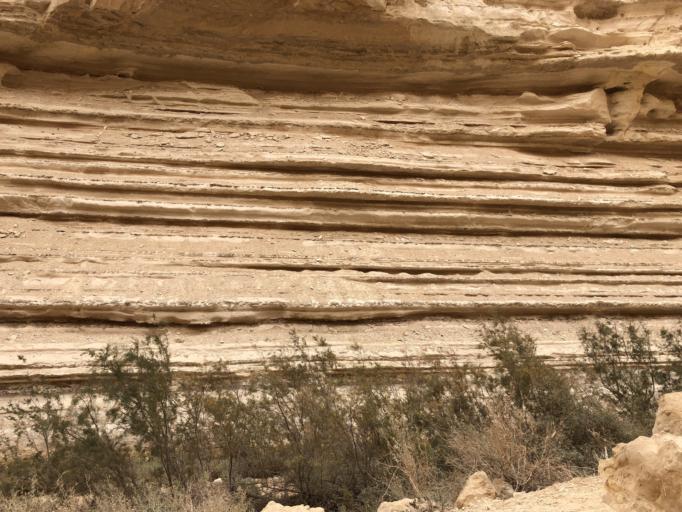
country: IL
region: Southern District
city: Midreshet Ben-Gurion
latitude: 30.8279
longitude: 34.7658
